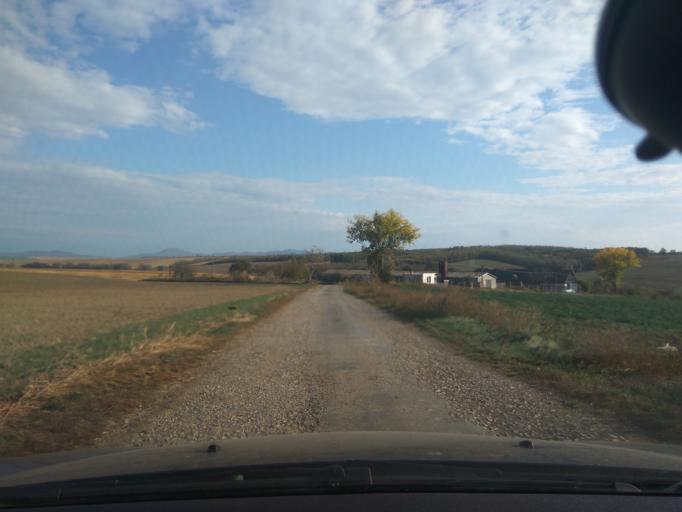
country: SK
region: Trnavsky
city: Hlohovec
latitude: 48.4468
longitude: 17.9247
